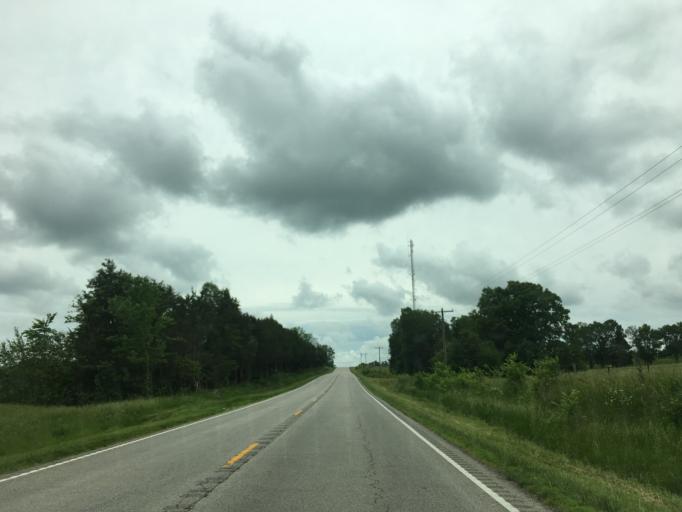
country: US
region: Missouri
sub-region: Gasconade County
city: Owensville
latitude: 38.4934
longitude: -91.4620
